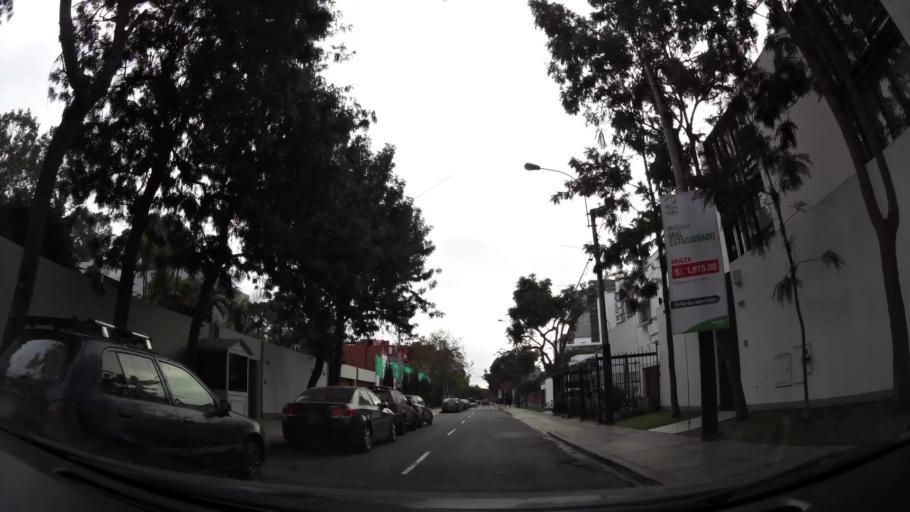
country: PE
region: Lima
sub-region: Lima
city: San Isidro
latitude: -12.1039
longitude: -77.0418
